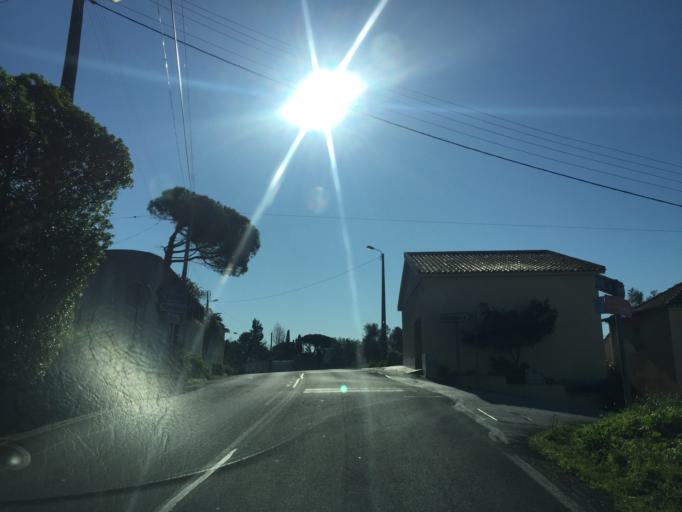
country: PT
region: Lisbon
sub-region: Sintra
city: Pero Pinheiro
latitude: 38.8353
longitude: -9.3097
